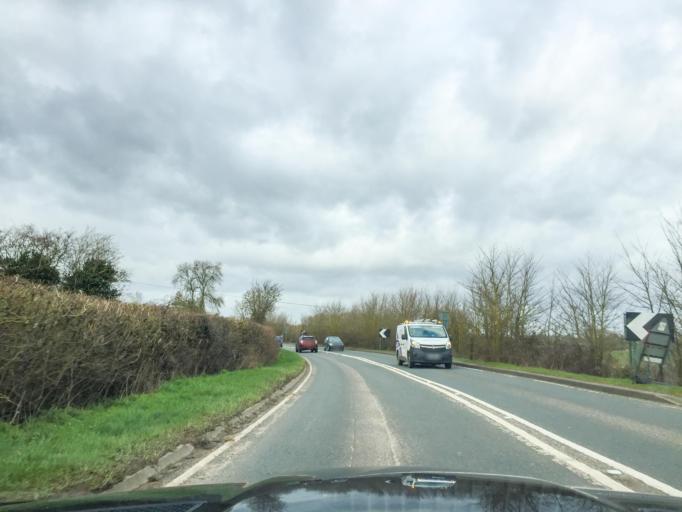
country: GB
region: England
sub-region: Warwickshire
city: Shipston on Stour
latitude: 52.0700
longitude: -1.6195
